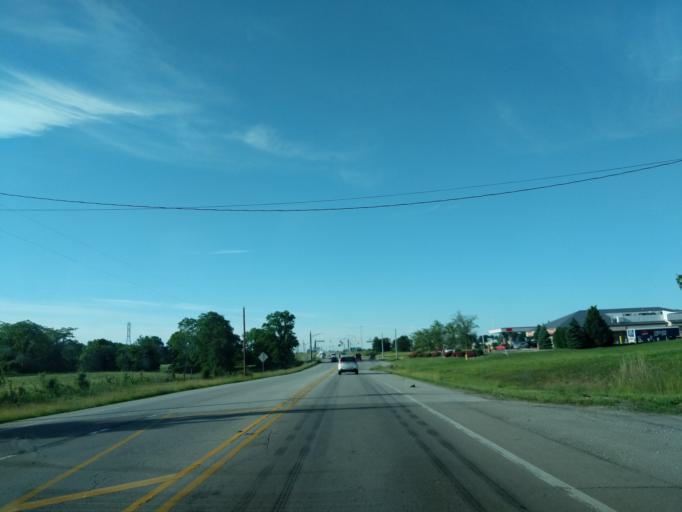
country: US
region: Indiana
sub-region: Hancock County
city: Greenfield
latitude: 39.8280
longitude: -85.7702
